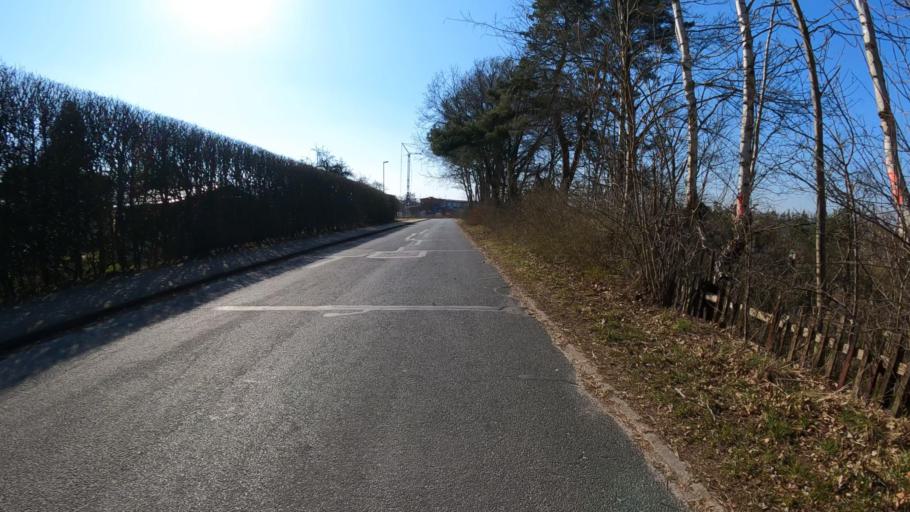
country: DE
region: Lower Saxony
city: Buchholz in der Nordheide
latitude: 53.3227
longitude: 9.8693
